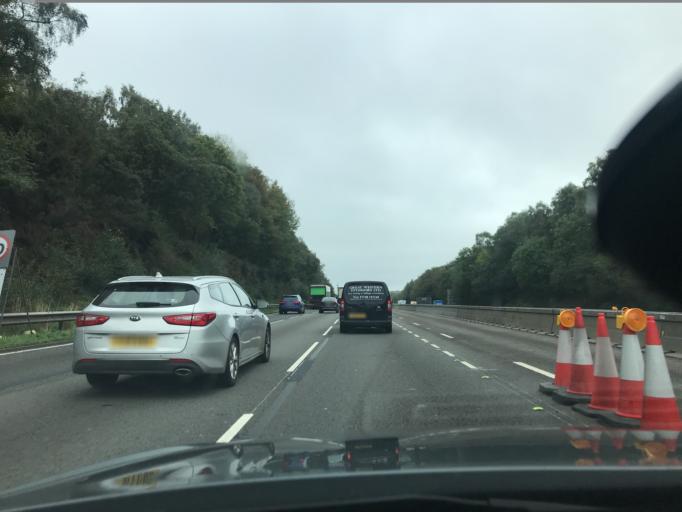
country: GB
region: England
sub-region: Staffordshire
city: Newcastle under Lyme
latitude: 52.9613
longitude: -2.2205
